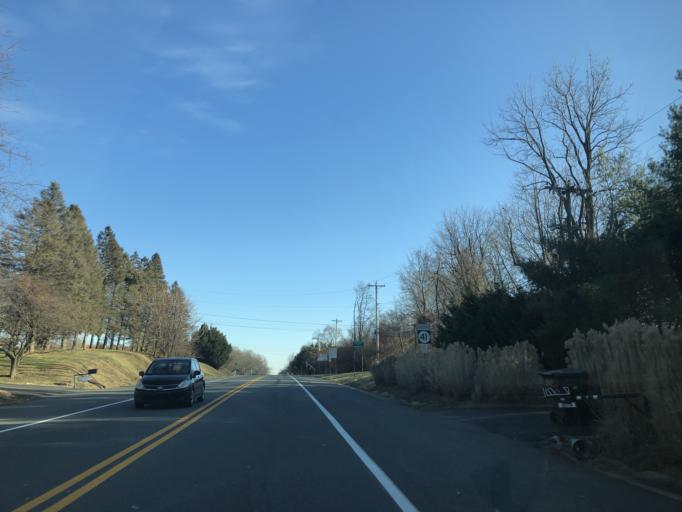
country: US
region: Delaware
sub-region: New Castle County
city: Hockessin
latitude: 39.7939
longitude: -75.7121
